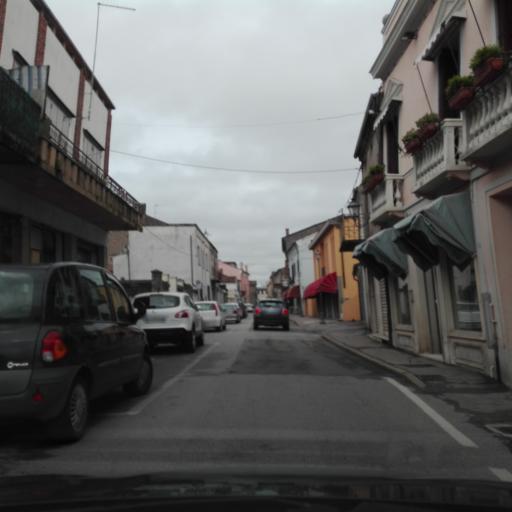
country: IT
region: Veneto
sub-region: Provincia di Rovigo
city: Lendinara
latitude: 45.0834
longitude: 11.6037
